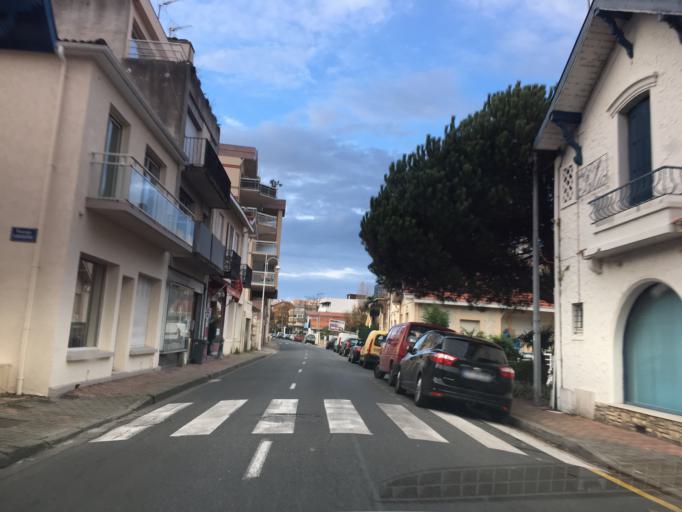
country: FR
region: Aquitaine
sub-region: Departement de la Gironde
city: Arcachon
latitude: 44.6614
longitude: -1.1565
